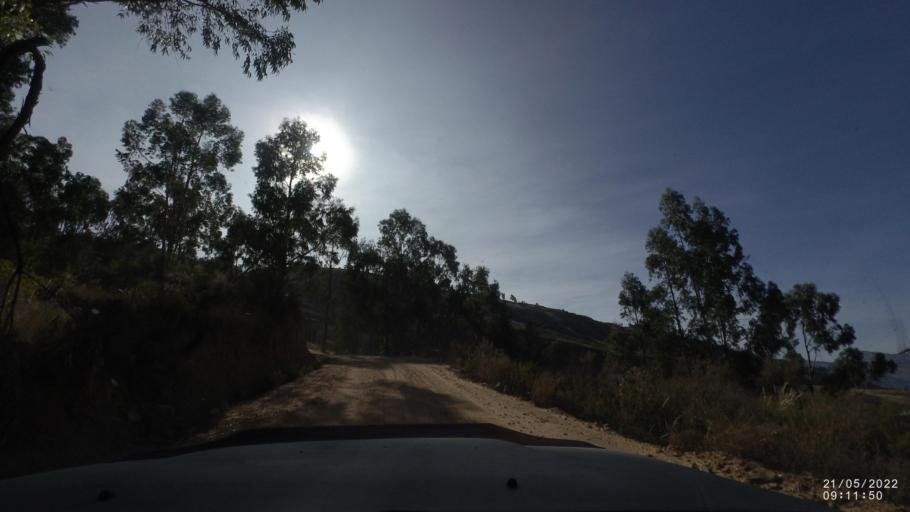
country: BO
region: Cochabamba
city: Cochabamba
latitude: -17.3706
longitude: -66.0218
